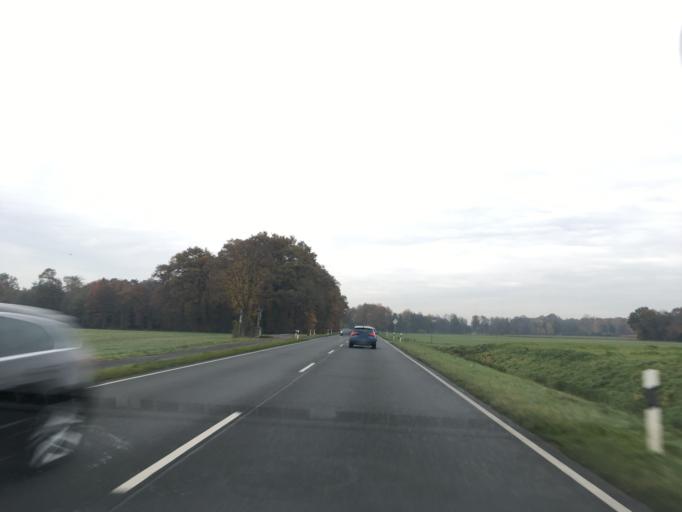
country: DE
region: North Rhine-Westphalia
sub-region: Regierungsbezirk Munster
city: Ostbevern
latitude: 52.0148
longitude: 7.8177
